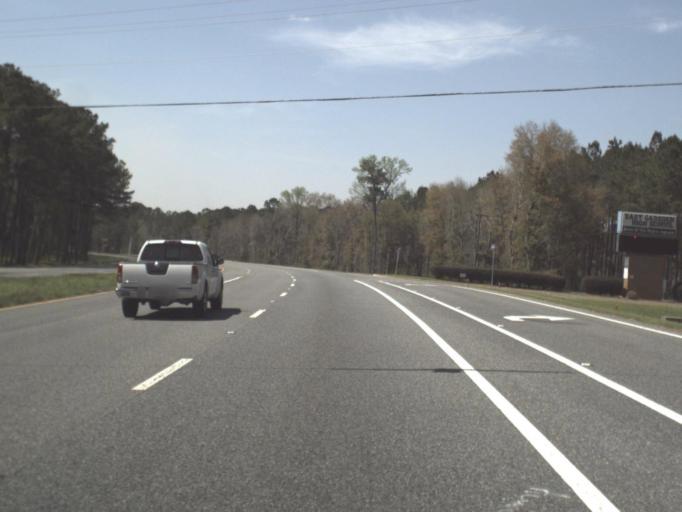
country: US
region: Florida
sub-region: Gadsden County
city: Midway
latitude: 30.5511
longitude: -84.4899
